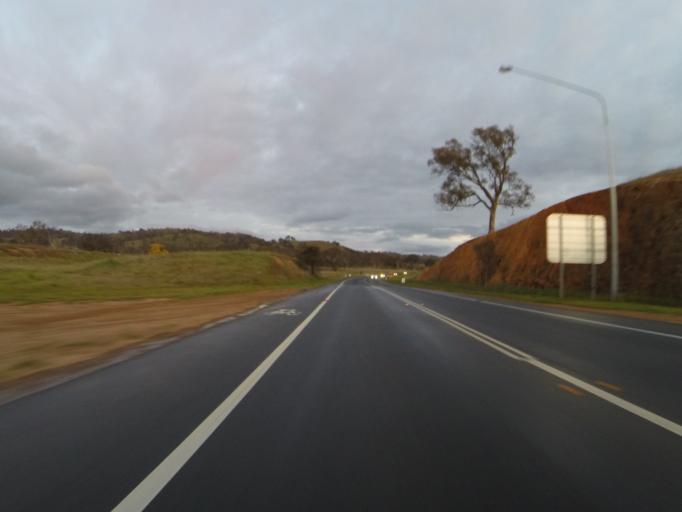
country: AU
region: Australian Capital Territory
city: Kaleen
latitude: -35.2009
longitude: 149.1661
